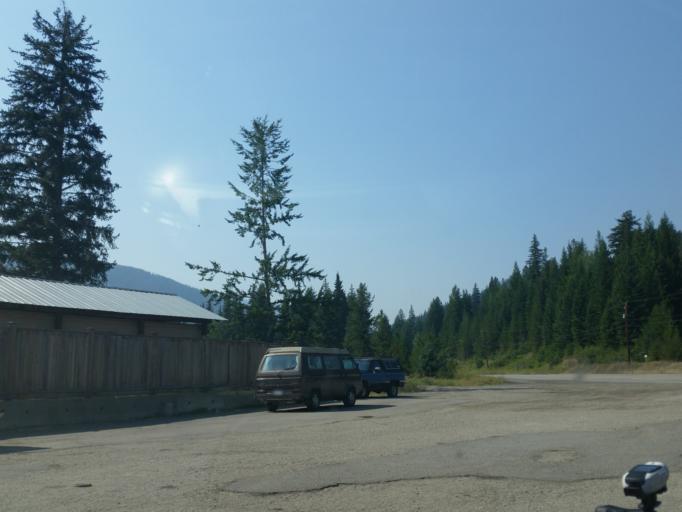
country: CA
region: British Columbia
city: Princeton
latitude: 49.1355
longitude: -120.6186
